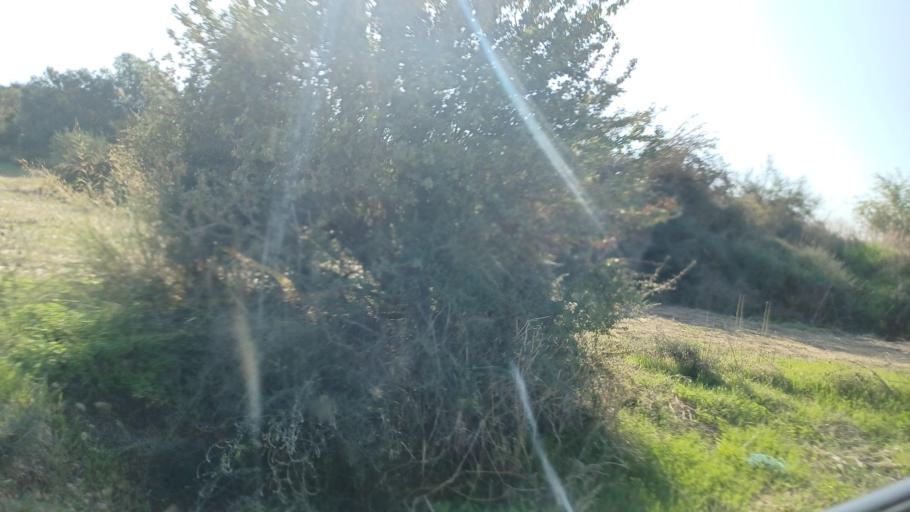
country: CY
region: Pafos
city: Polis
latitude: 35.0100
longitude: 32.4445
